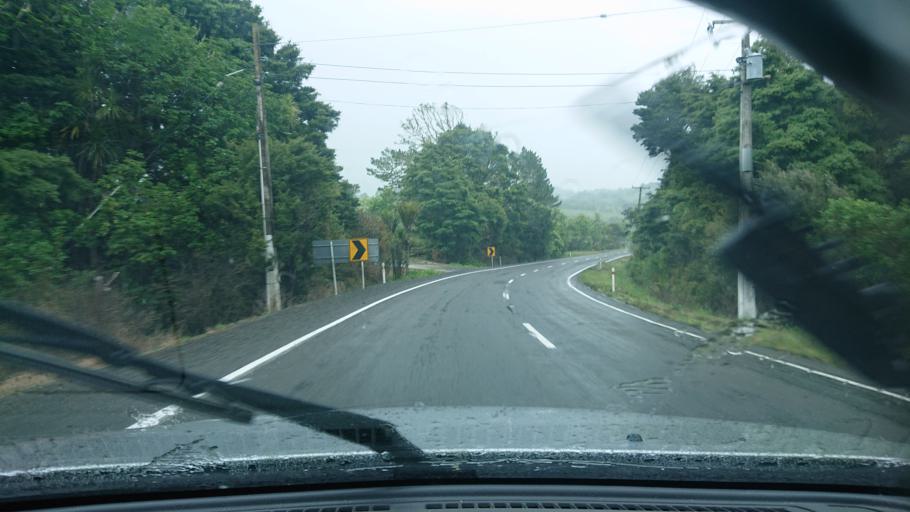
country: NZ
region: Auckland
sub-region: Auckland
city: Wellsford
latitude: -36.3136
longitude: 174.4949
